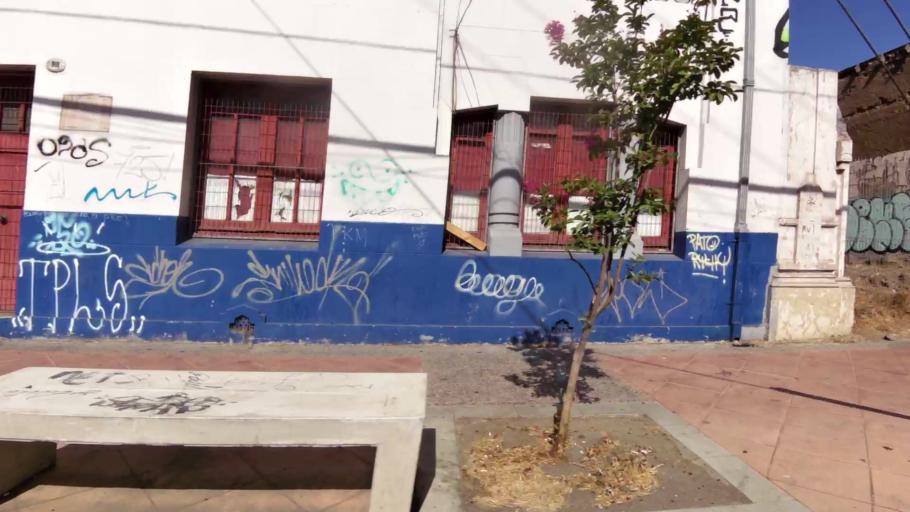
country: CL
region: Maule
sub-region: Provincia de Talca
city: Talca
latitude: -35.4286
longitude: -71.6655
